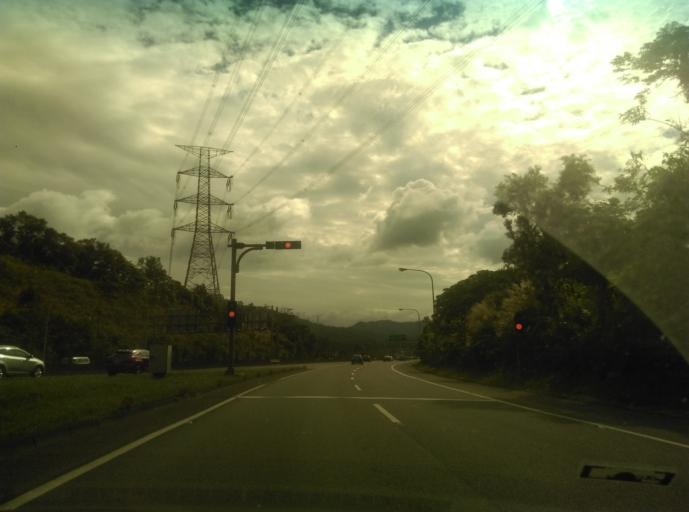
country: TW
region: Taipei
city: Taipei
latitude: 25.0681
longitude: 121.6440
